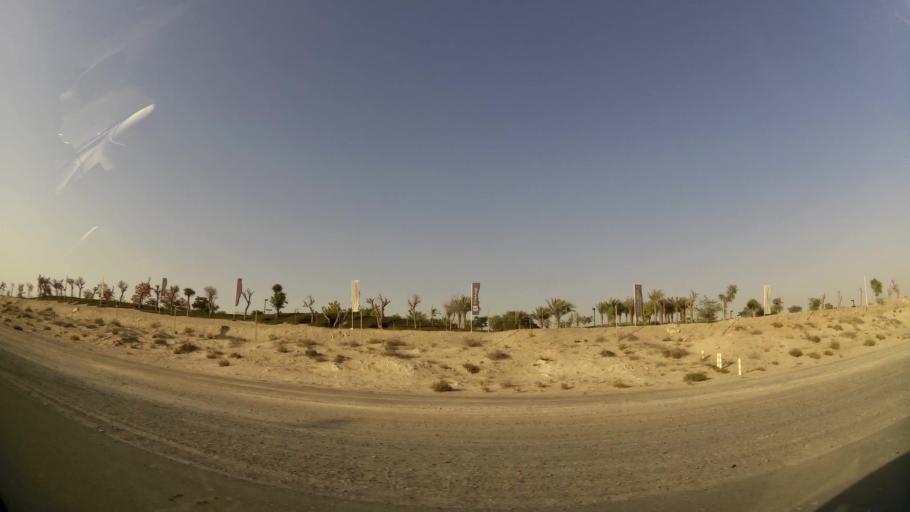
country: AE
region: Dubai
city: Dubai
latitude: 25.0931
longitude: 55.2441
